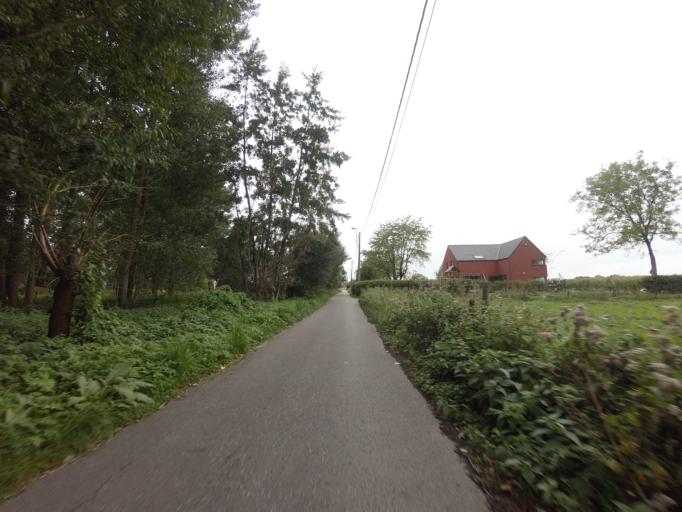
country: BE
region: Flanders
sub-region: Provincie Vlaams-Brabant
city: Meise
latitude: 50.9608
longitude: 4.3278
